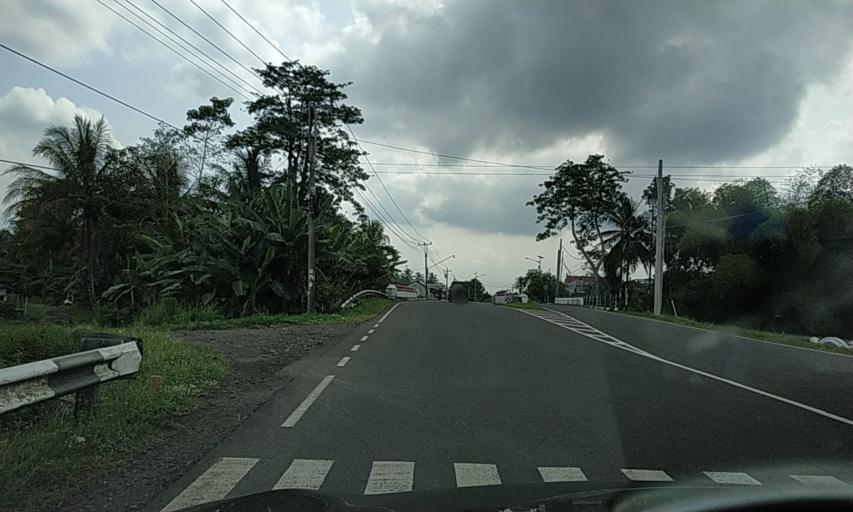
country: ID
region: Central Java
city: Sogati
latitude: -7.3334
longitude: 108.6739
